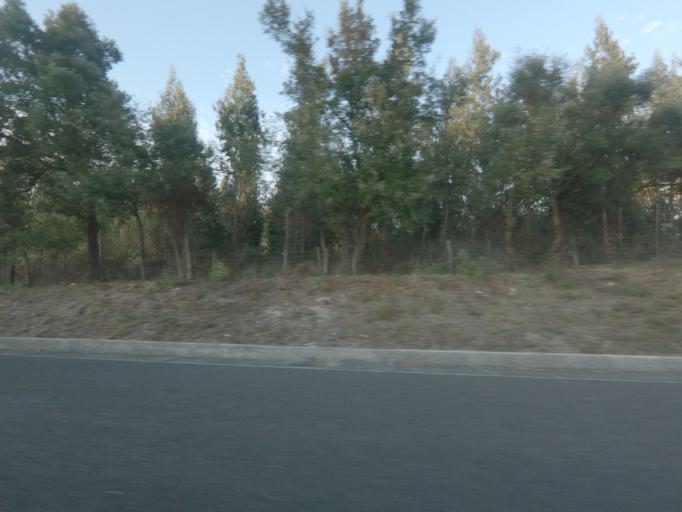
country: PT
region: Leiria
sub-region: Leiria
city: Santa Catarina da Serra
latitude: 39.7067
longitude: -8.7065
